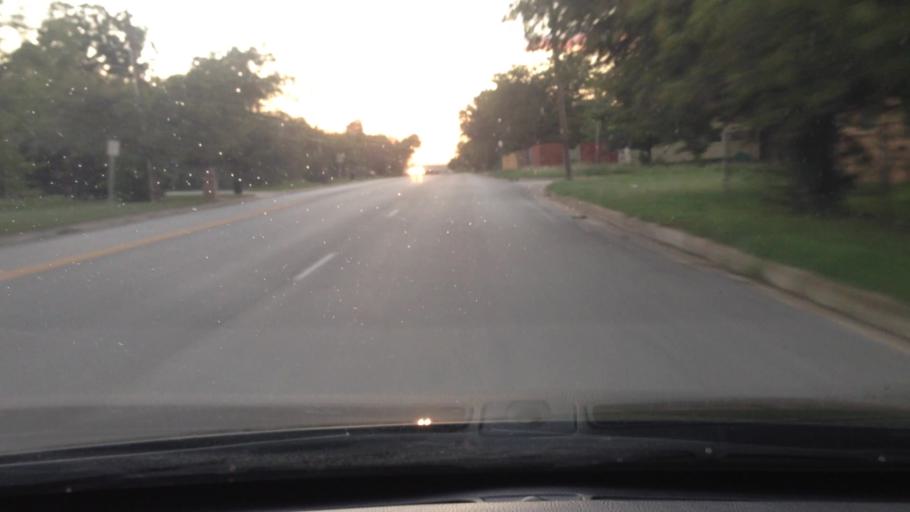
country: US
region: Texas
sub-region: Tarrant County
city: White Settlement
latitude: 32.7738
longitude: -97.4699
